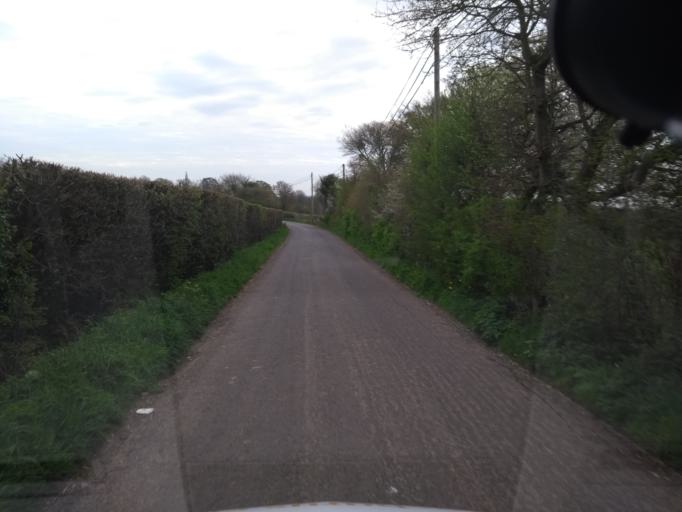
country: GB
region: England
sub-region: Somerset
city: Creech Saint Michael
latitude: 50.9836
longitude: -2.9718
